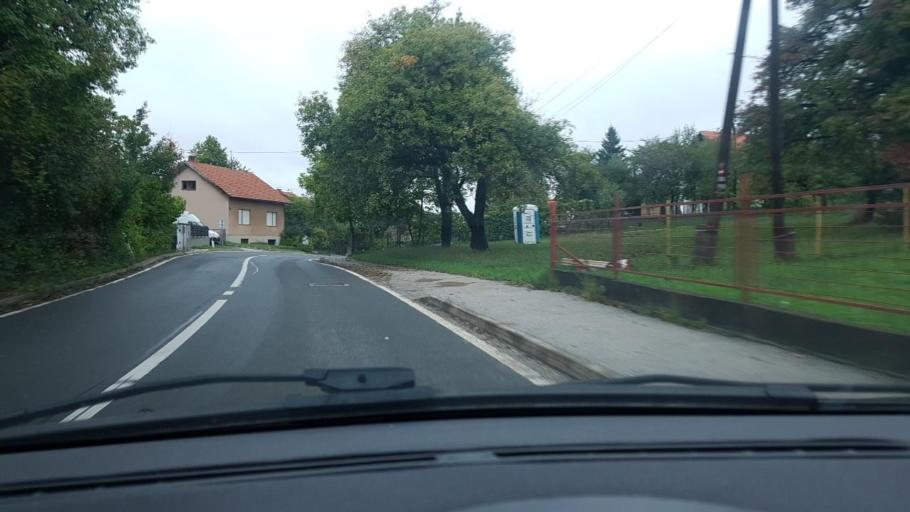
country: HR
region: Krapinsko-Zagorska
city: Marija Bistrica
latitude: 45.9664
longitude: 16.0951
